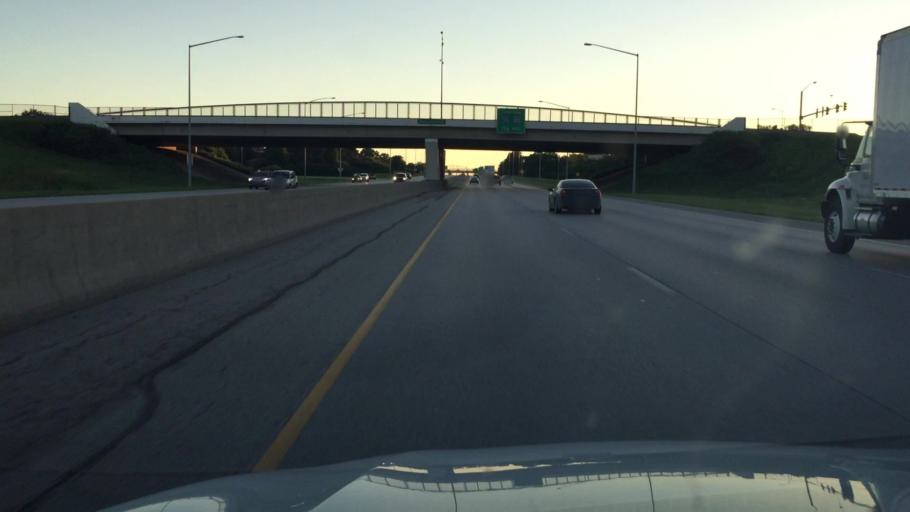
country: US
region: Iowa
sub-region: Polk County
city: Clive
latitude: 41.5923
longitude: -93.7505
